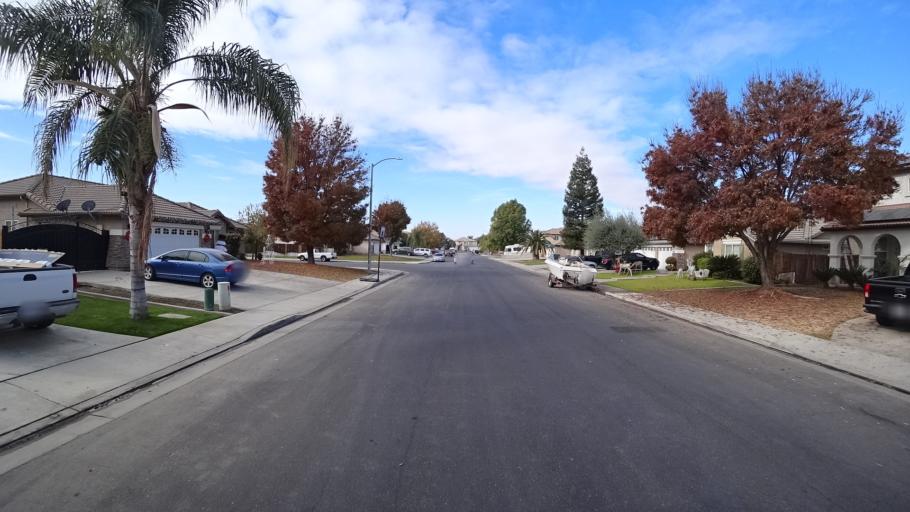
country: US
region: California
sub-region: Kern County
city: Greenacres
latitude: 35.3003
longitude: -119.1206
